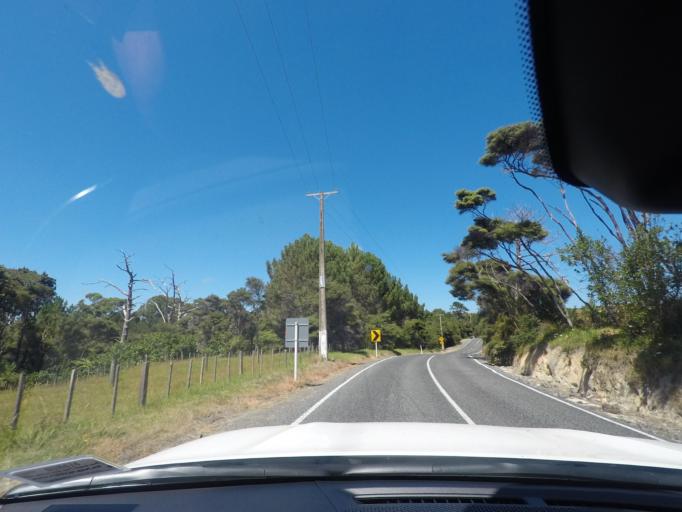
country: NZ
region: Auckland
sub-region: Auckland
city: Parakai
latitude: -36.5804
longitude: 174.3358
